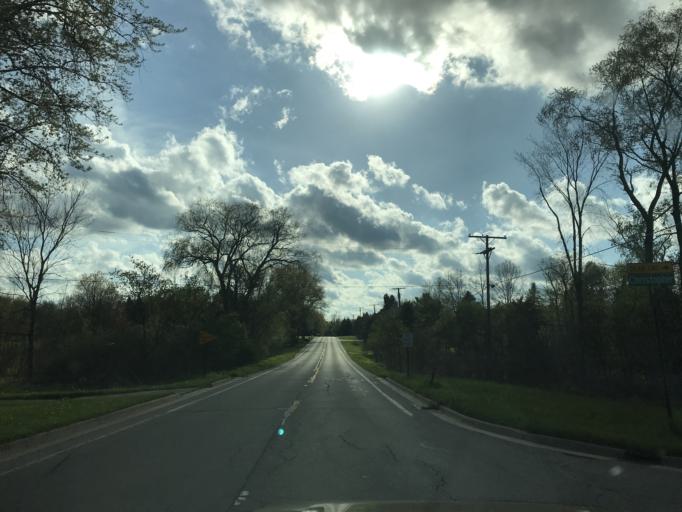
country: US
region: Michigan
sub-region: Livingston County
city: Brighton
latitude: 42.5454
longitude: -83.7399
